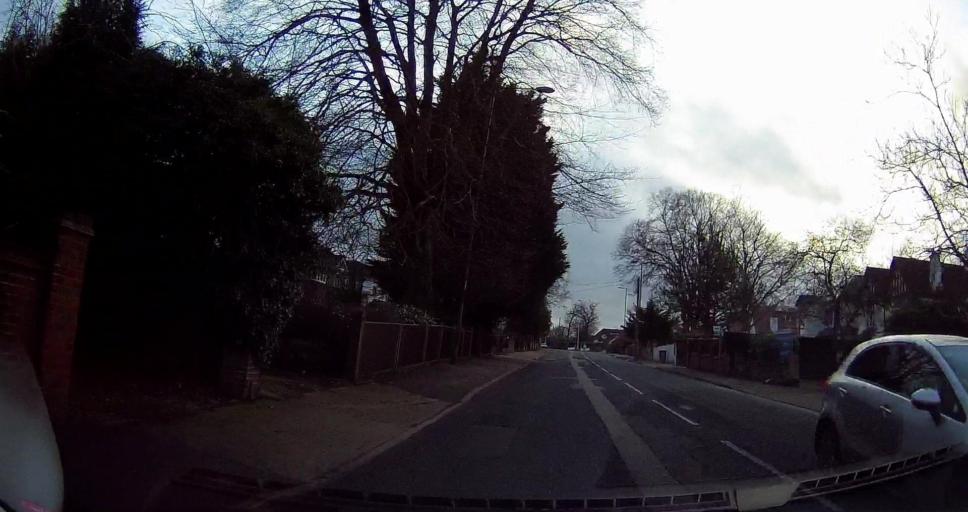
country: GB
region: England
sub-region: Kent
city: Chatham
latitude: 51.3621
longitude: 0.5179
